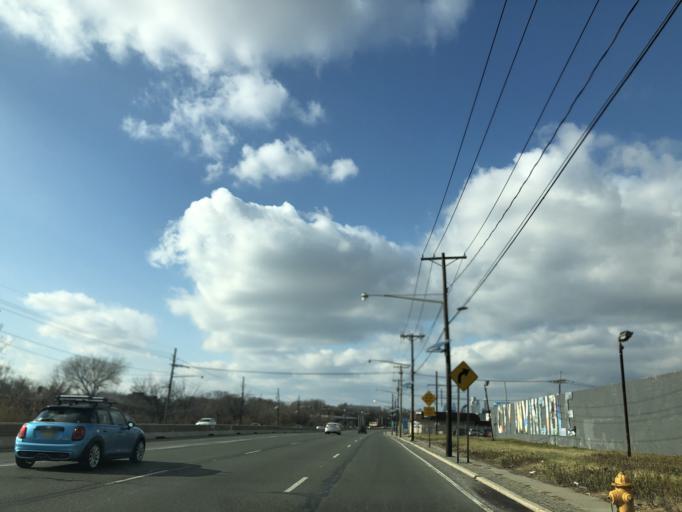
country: US
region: New Jersey
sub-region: Camden County
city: Wood-Lynne
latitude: 39.9408
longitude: -75.0997
